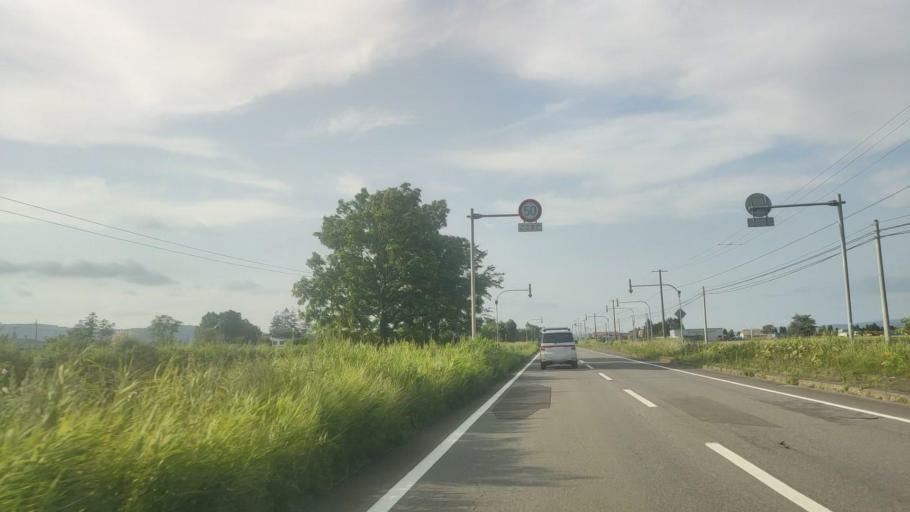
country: JP
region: Hokkaido
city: Chitose
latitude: 42.9560
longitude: 141.7987
